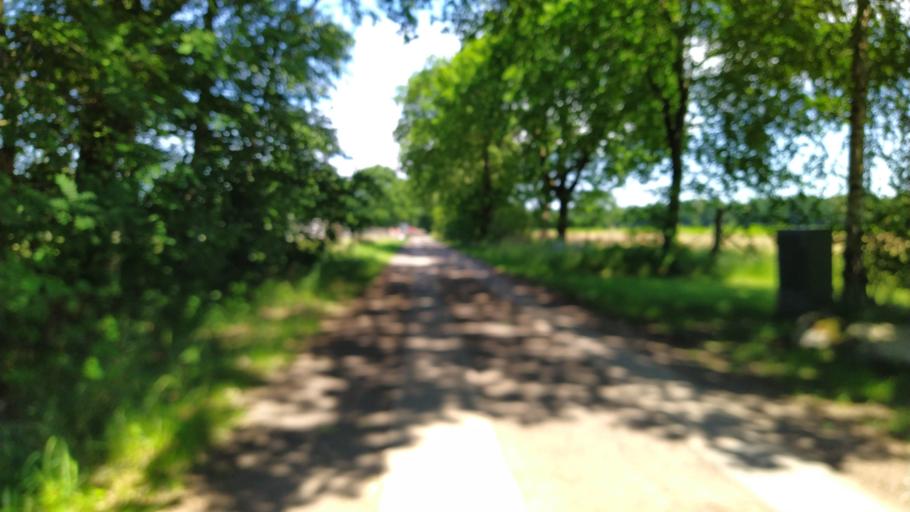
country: DE
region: Lower Saxony
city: Bargstedt
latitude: 53.4888
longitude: 9.4351
